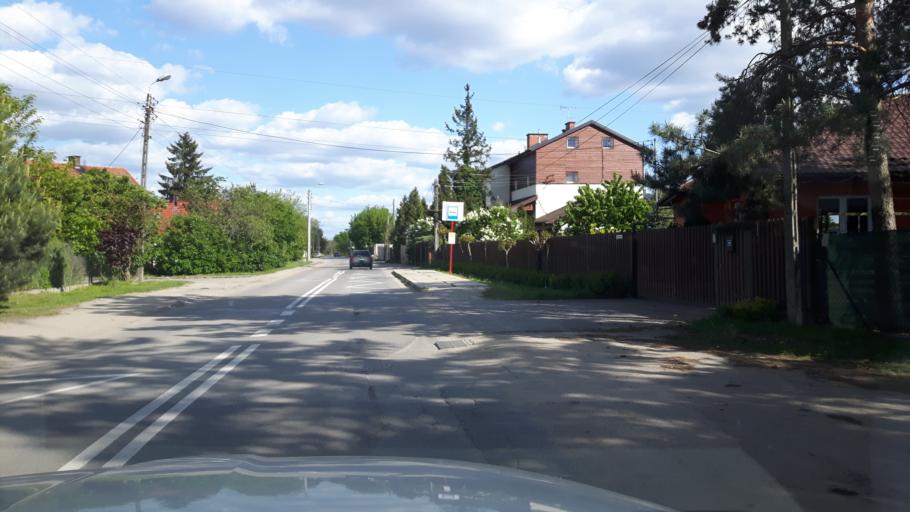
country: PL
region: Masovian Voivodeship
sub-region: Powiat wolominski
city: Marki
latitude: 52.3201
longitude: 21.1197
